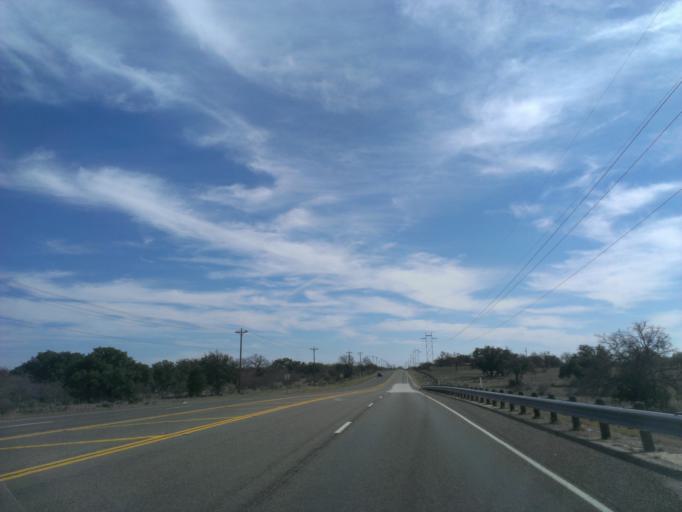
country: US
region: Texas
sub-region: Burnet County
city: Granite Shoals
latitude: 30.6152
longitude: -98.3876
